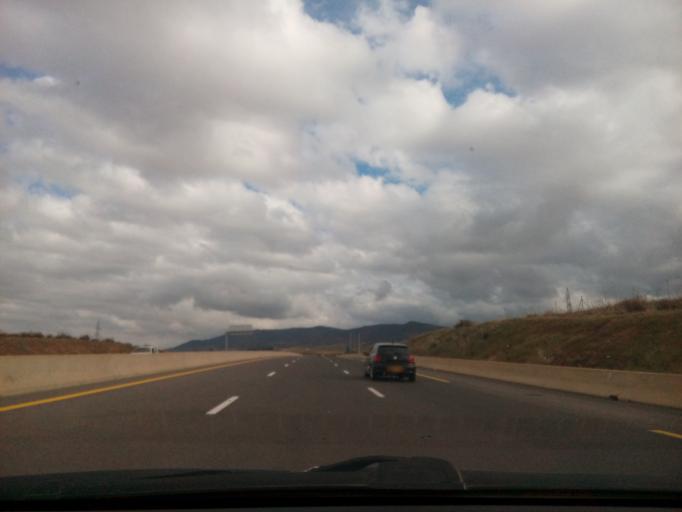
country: DZ
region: Tlemcen
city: Bensekrane
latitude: 34.9870
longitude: -1.2256
